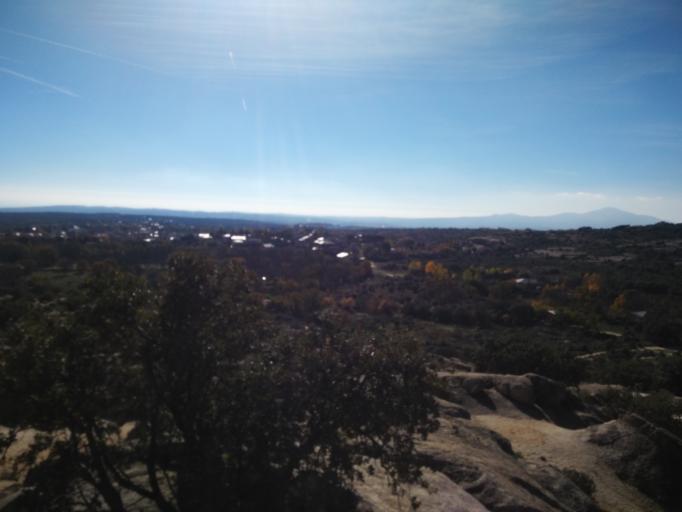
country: ES
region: Madrid
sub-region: Provincia de Madrid
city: La Cabrera
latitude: 40.8731
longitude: -3.6199
